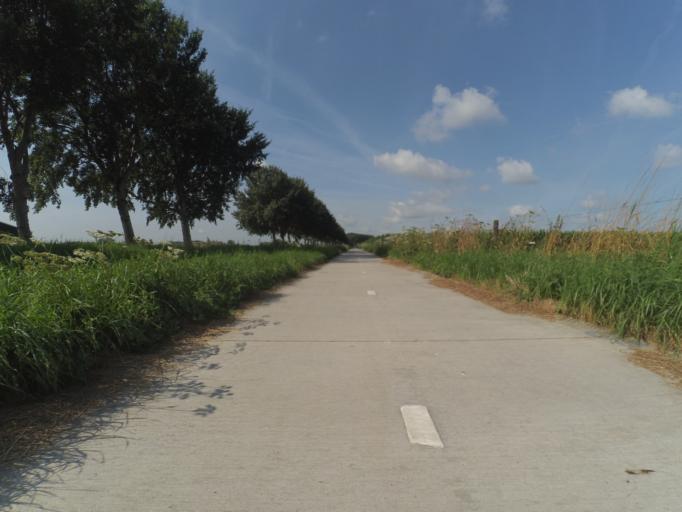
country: NL
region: Utrecht
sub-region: Gemeente Houten
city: Houten
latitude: 52.0205
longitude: 5.2130
